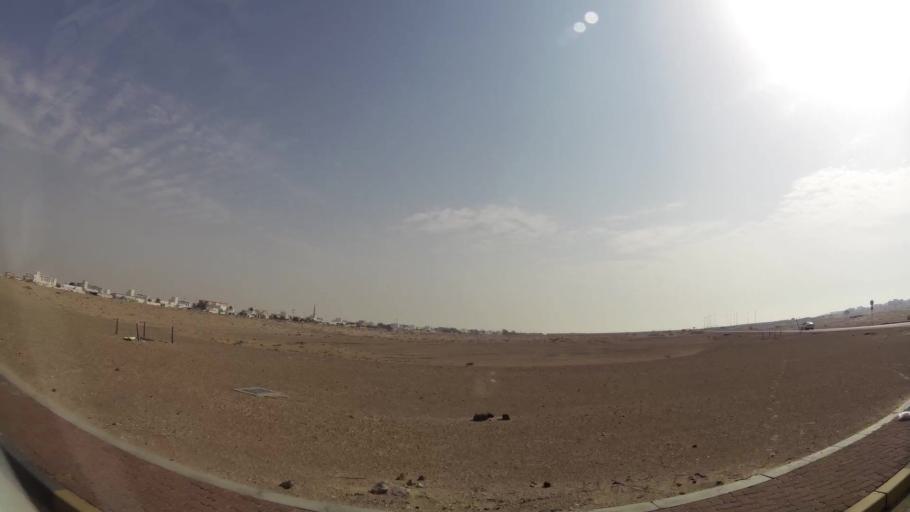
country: AE
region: Abu Dhabi
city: Abu Dhabi
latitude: 24.2709
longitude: 54.6846
